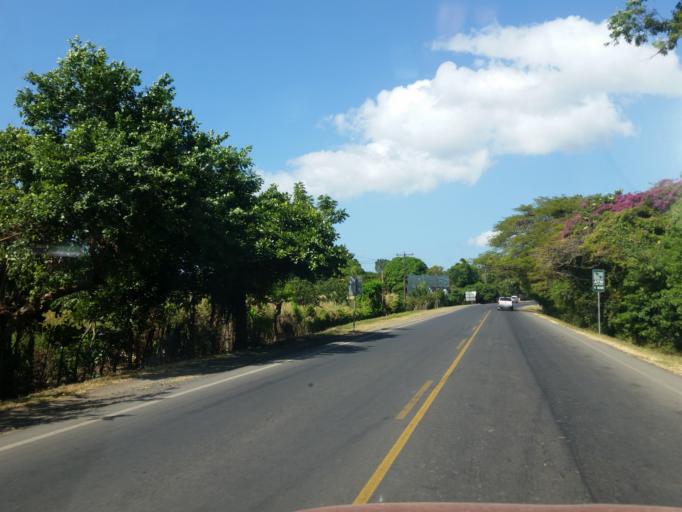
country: NI
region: Granada
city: Nandaime
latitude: 11.7540
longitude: -86.0425
